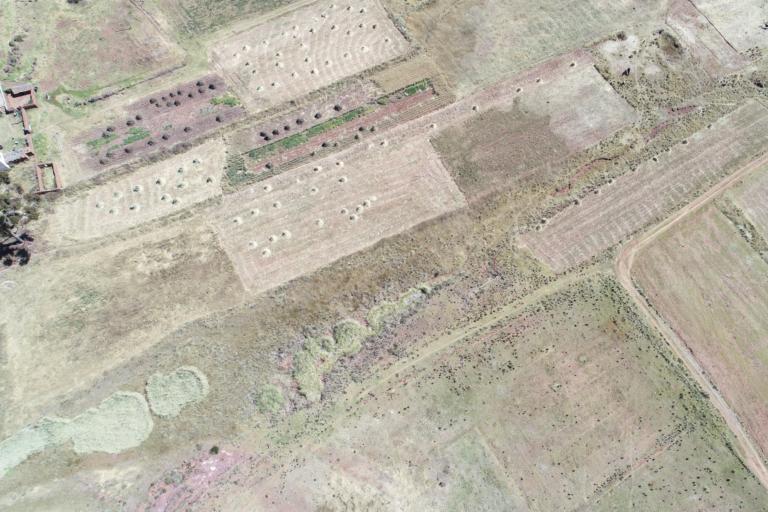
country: BO
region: La Paz
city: Tiahuanaco
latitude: -16.6027
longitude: -68.7727
